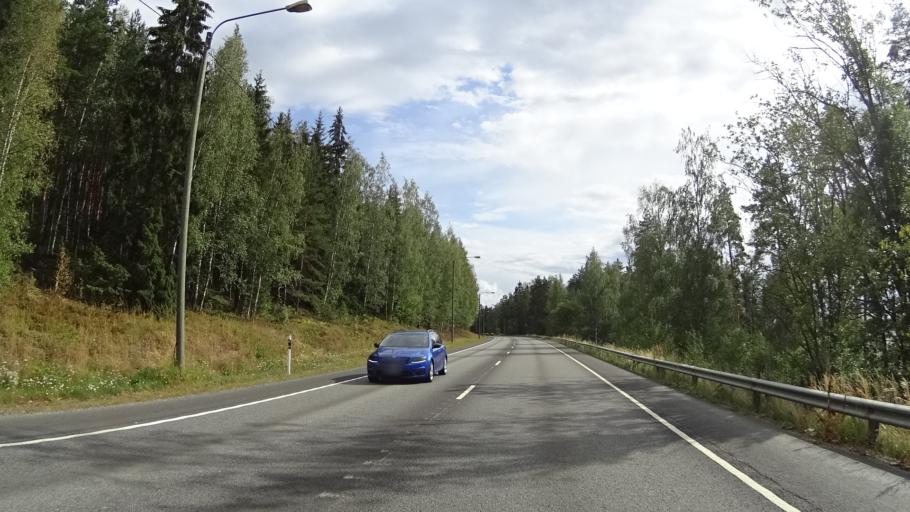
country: FI
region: Pirkanmaa
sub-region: Tampere
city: Kangasala
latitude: 61.4336
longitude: 24.1269
